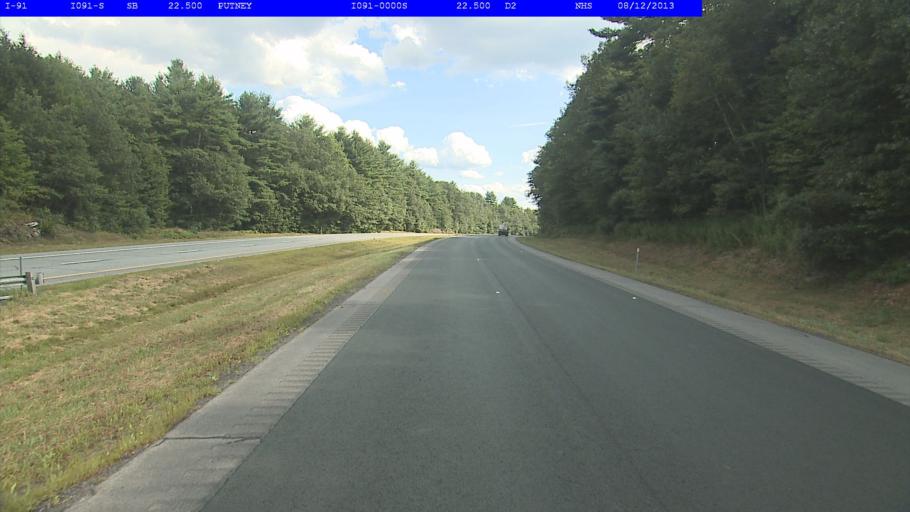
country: US
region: New Hampshire
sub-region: Cheshire County
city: Westmoreland
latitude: 43.0057
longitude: -72.4688
